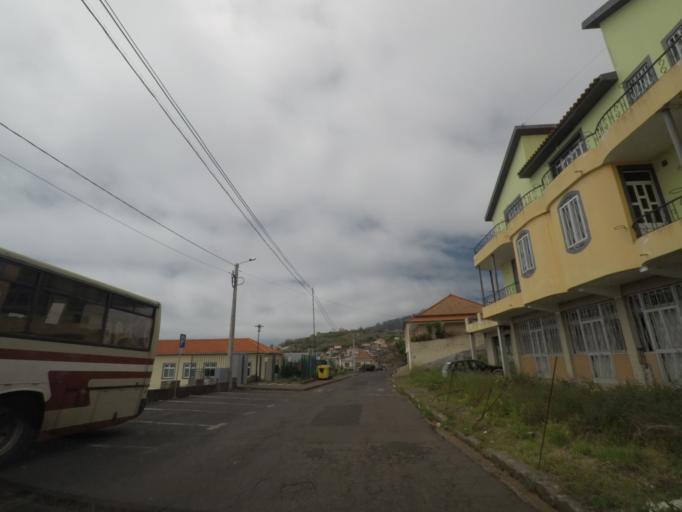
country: PT
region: Madeira
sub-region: Calheta
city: Arco da Calheta
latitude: 32.7122
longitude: -17.1205
